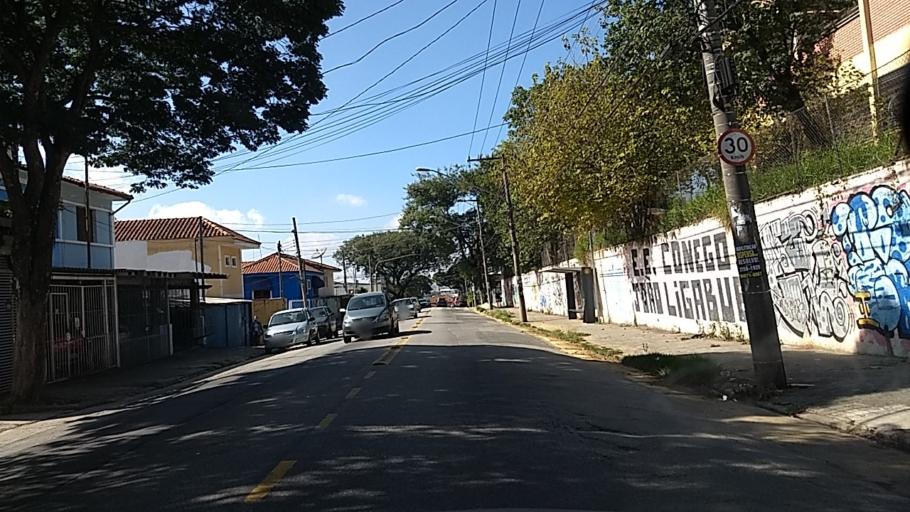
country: BR
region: Sao Paulo
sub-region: Guarulhos
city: Guarulhos
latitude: -23.4813
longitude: -46.5969
